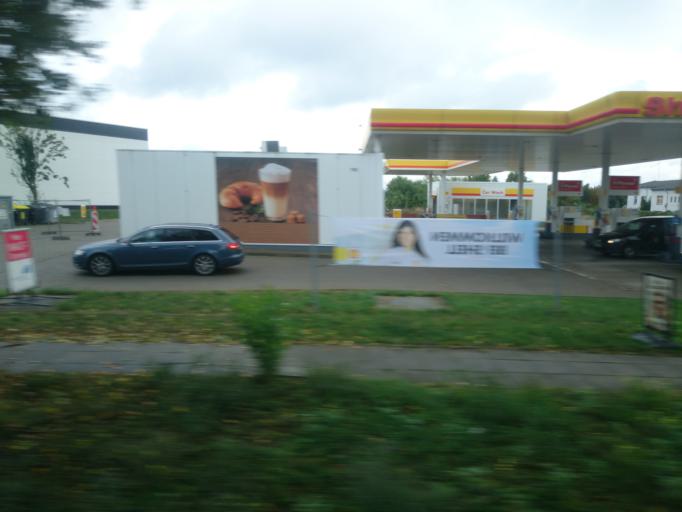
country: DE
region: Saxony-Anhalt
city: Halle (Saale)
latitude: 51.4958
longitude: 12.0110
